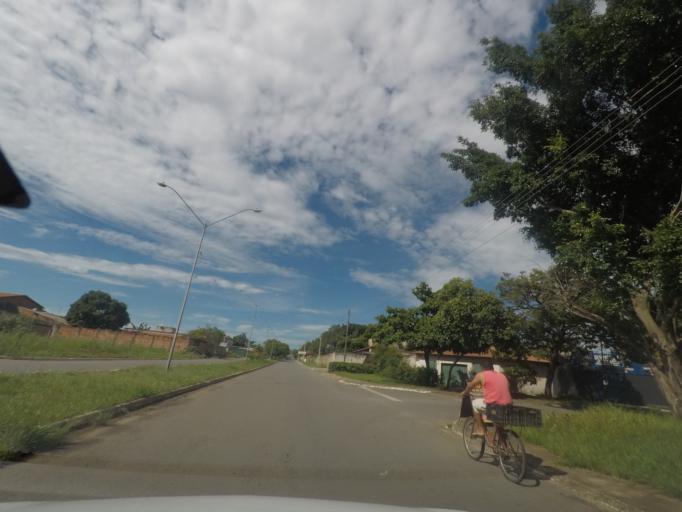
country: BR
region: Goias
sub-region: Aparecida De Goiania
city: Aparecida de Goiania
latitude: -16.8174
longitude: -49.2901
